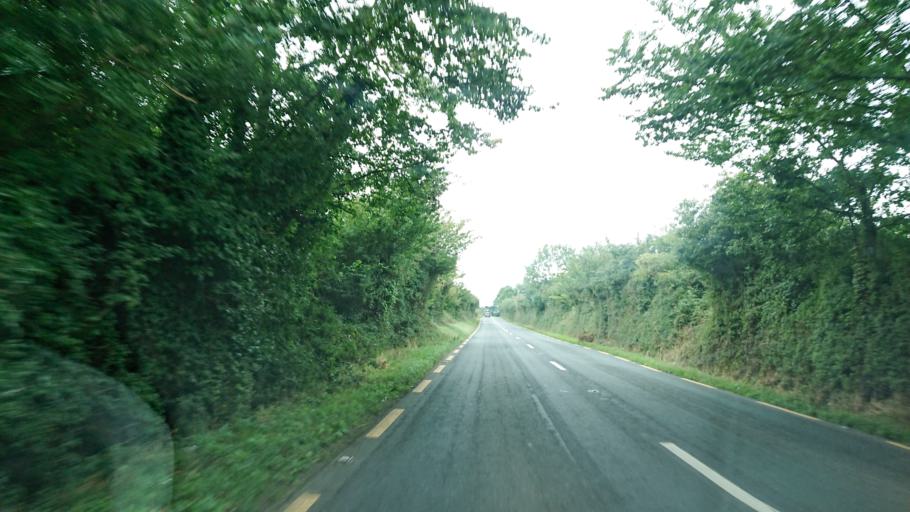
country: IE
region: Munster
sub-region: Waterford
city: Dungarvan
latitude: 52.1105
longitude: -7.6875
